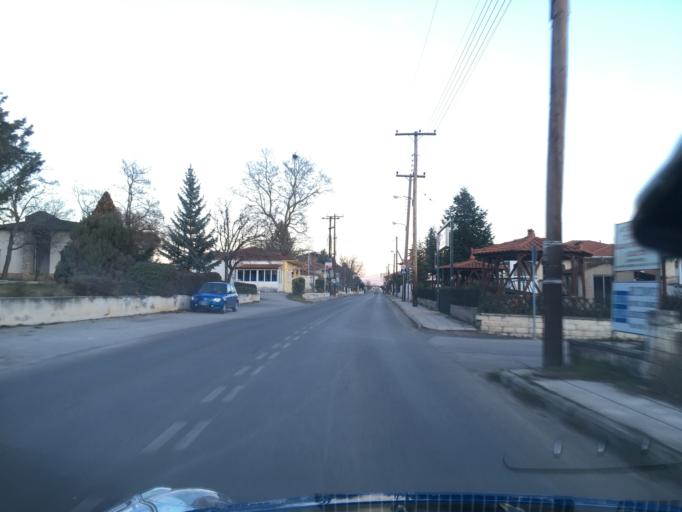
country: GR
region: West Macedonia
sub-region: Nomos Kozanis
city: Kozani
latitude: 40.2707
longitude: 21.7770
